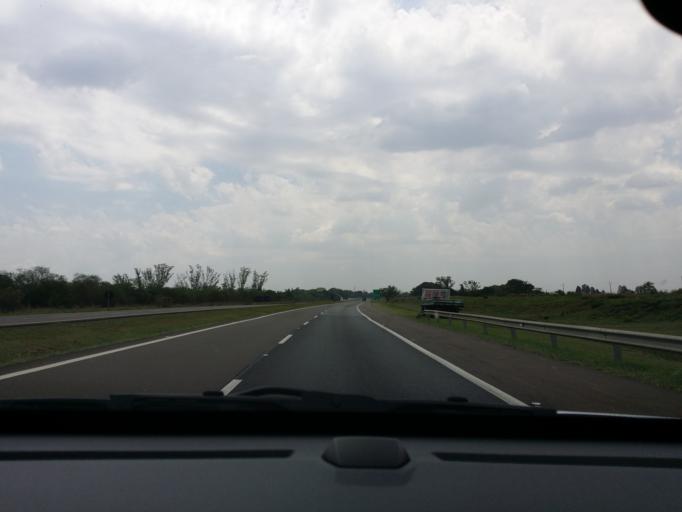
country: BR
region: Sao Paulo
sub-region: Iracemapolis
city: Iracemapolis
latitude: -22.6085
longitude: -47.4598
